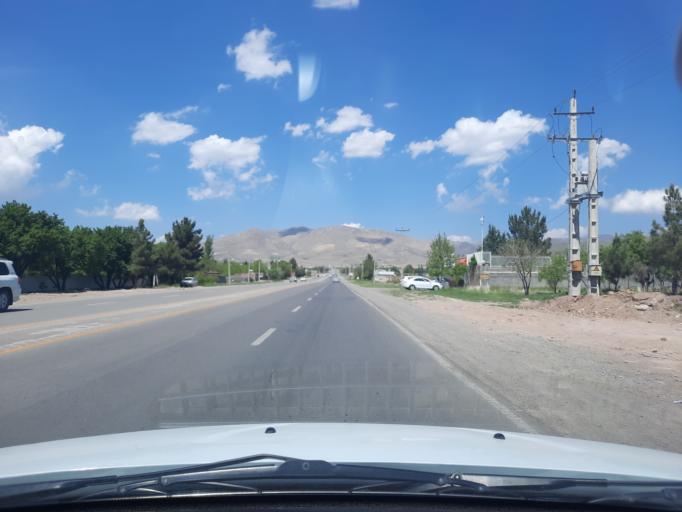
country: IR
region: Qazvin
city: Alvand
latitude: 36.3061
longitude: 50.1444
